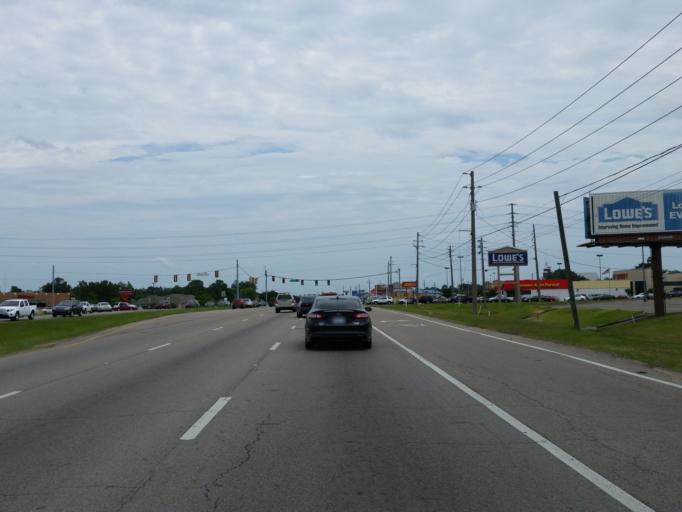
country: US
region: Mississippi
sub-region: Lamar County
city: West Hattiesburg
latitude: 31.3221
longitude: -89.3751
